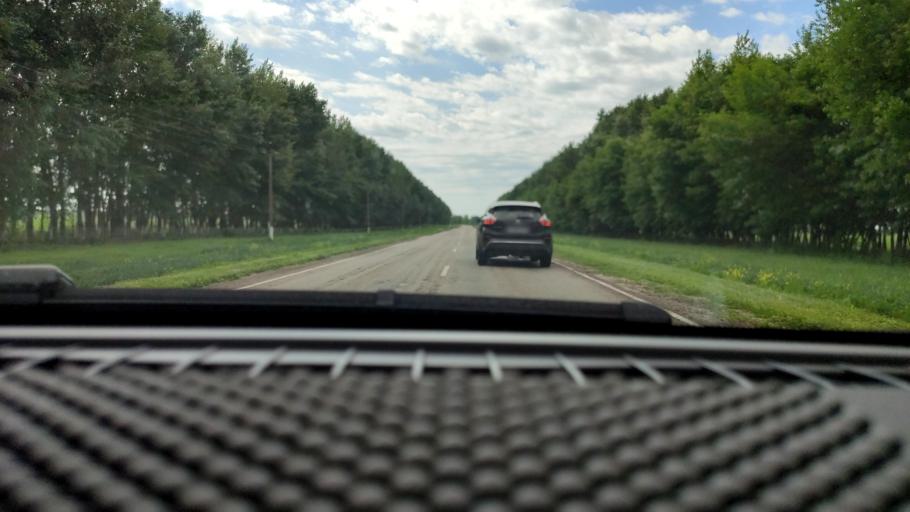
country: RU
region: Voronezj
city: Panino
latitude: 51.6544
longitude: 40.0732
